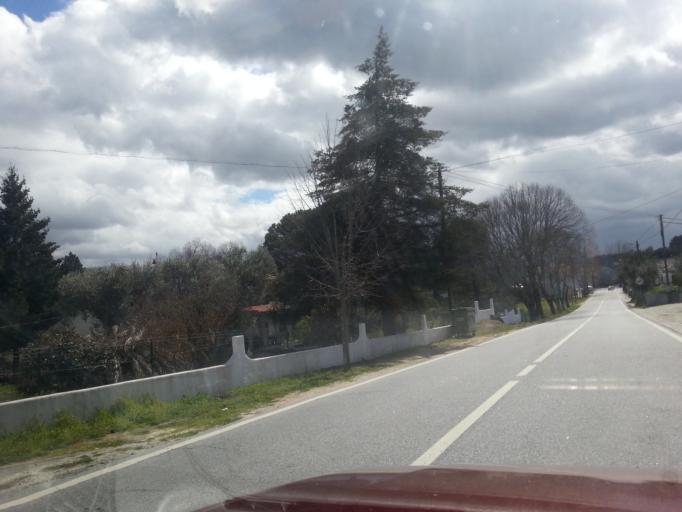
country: PT
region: Guarda
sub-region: Fornos de Algodres
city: Fornos de Algodres
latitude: 40.5918
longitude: -7.5362
